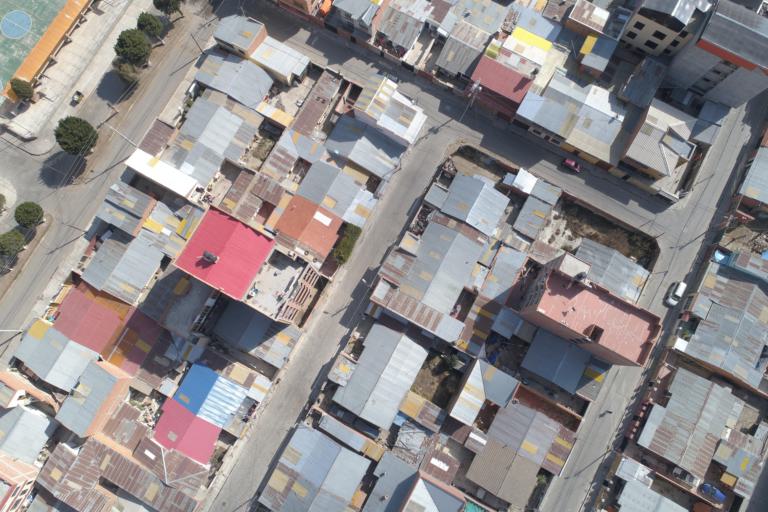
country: BO
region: La Paz
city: La Paz
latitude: -16.5285
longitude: -68.1498
